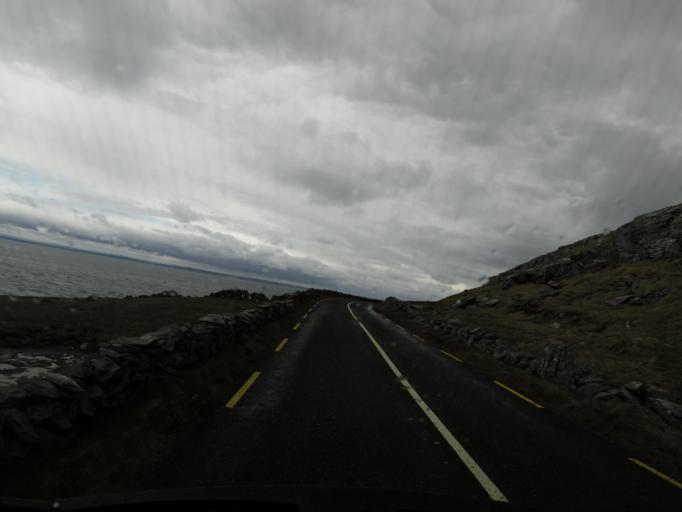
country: IE
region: Connaught
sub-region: County Galway
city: Bearna
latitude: 53.1514
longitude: -9.2683
